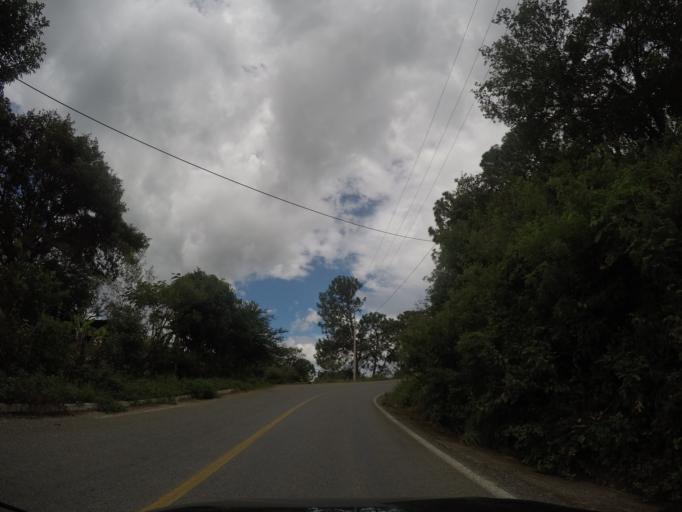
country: MX
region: Oaxaca
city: San Francisco Sola
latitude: 16.4883
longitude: -96.9843
